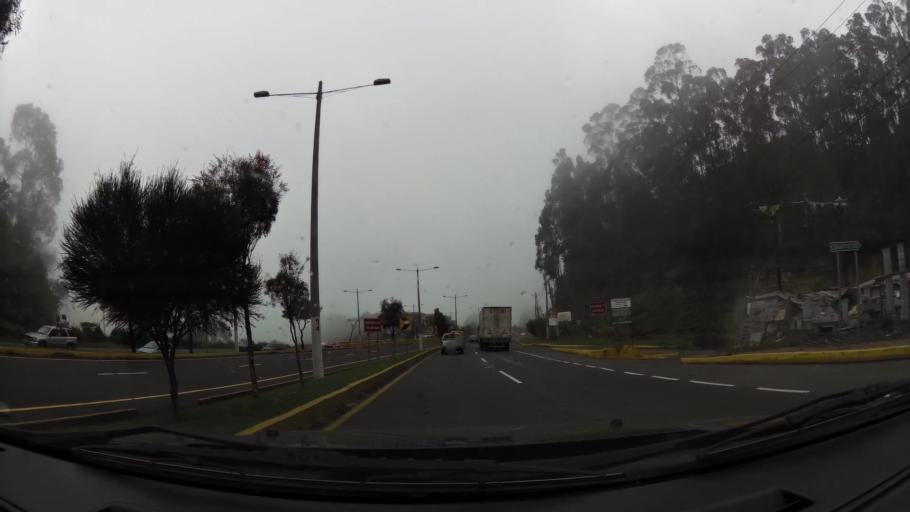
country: EC
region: Pichincha
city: Quito
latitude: -0.2489
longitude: -78.4834
